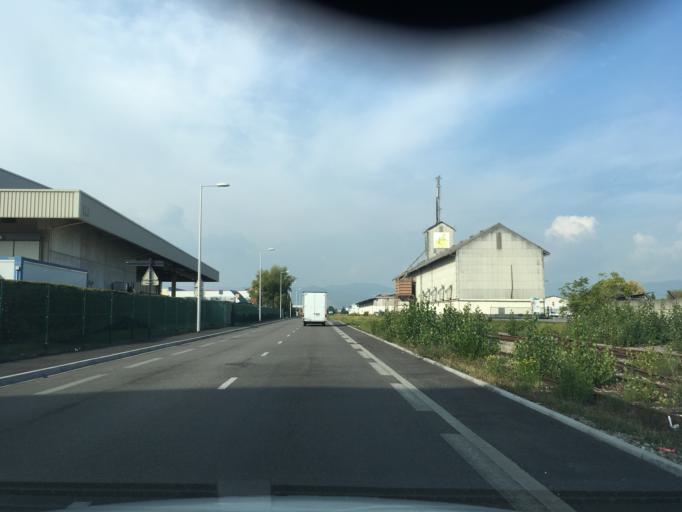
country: FR
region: Alsace
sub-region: Departement du Haut-Rhin
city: Colmar
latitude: 48.1029
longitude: 7.3749
